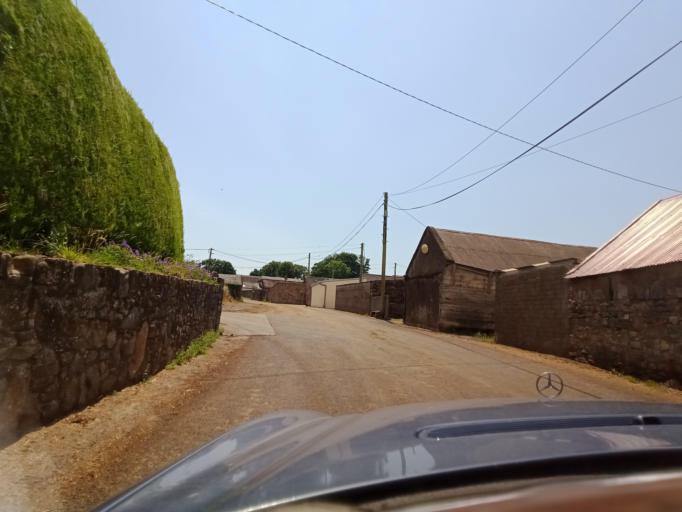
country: IE
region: Leinster
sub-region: Kilkenny
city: Mooncoin
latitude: 52.2705
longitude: -7.2280
